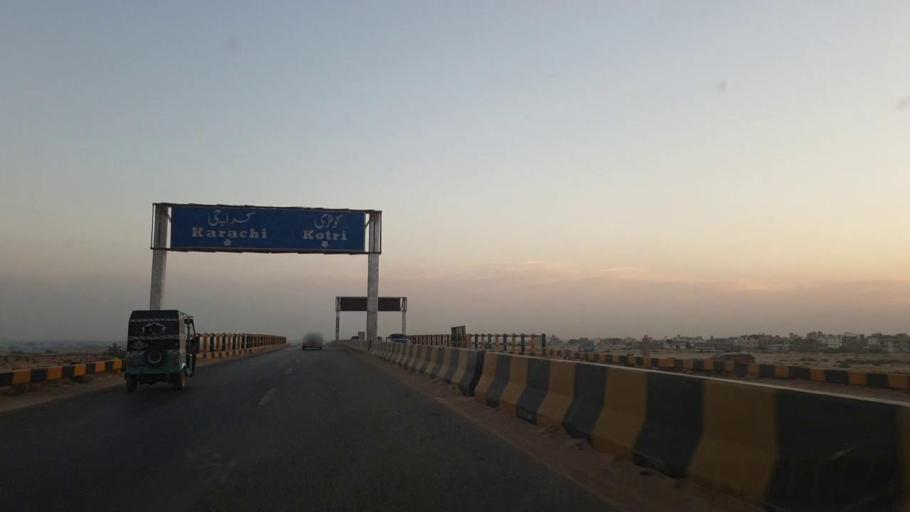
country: PK
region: Sindh
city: Jamshoro
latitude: 25.4003
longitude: 68.2726
